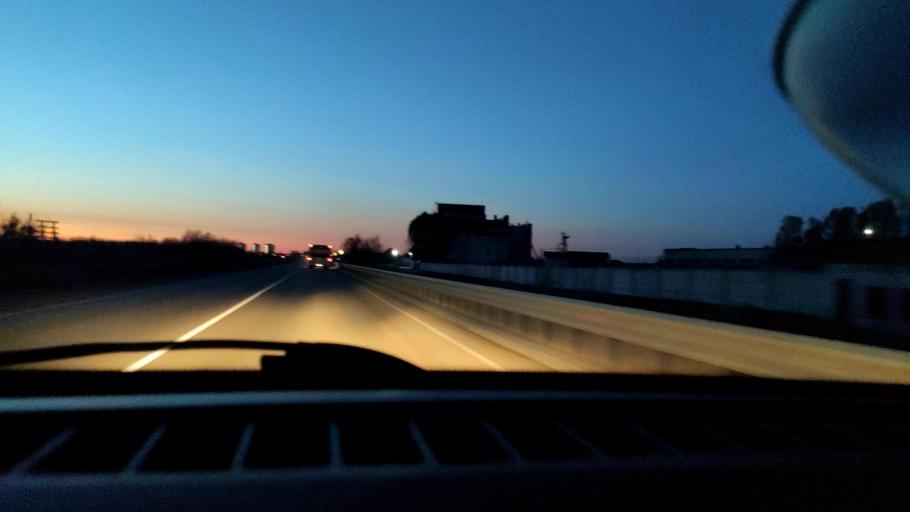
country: RU
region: Samara
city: Samara
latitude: 53.1270
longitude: 50.1120
